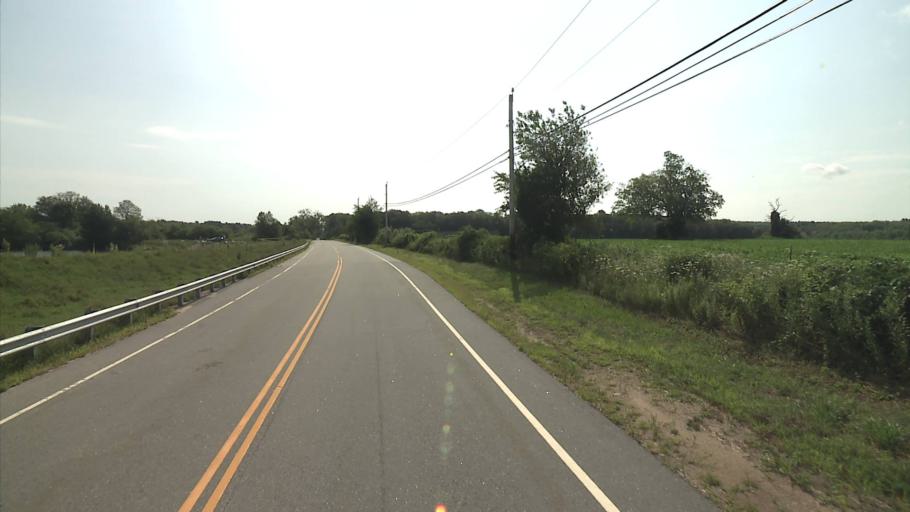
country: US
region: Connecticut
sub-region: New London County
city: Colchester
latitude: 41.5723
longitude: -72.2495
